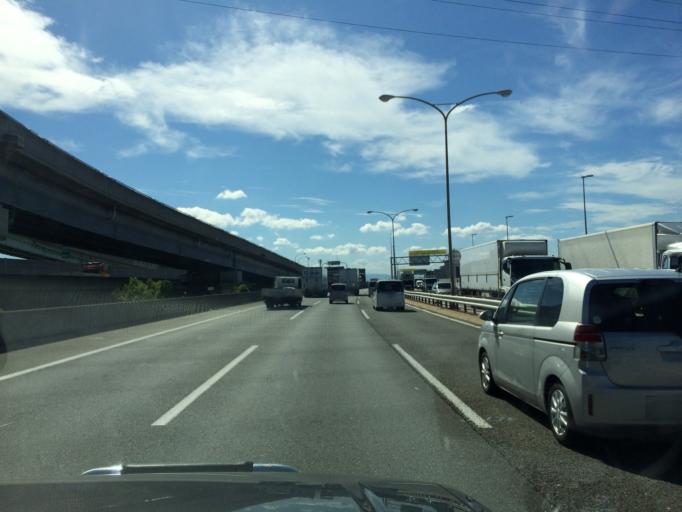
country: JP
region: Osaka
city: Daitocho
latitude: 34.6765
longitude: 135.5977
